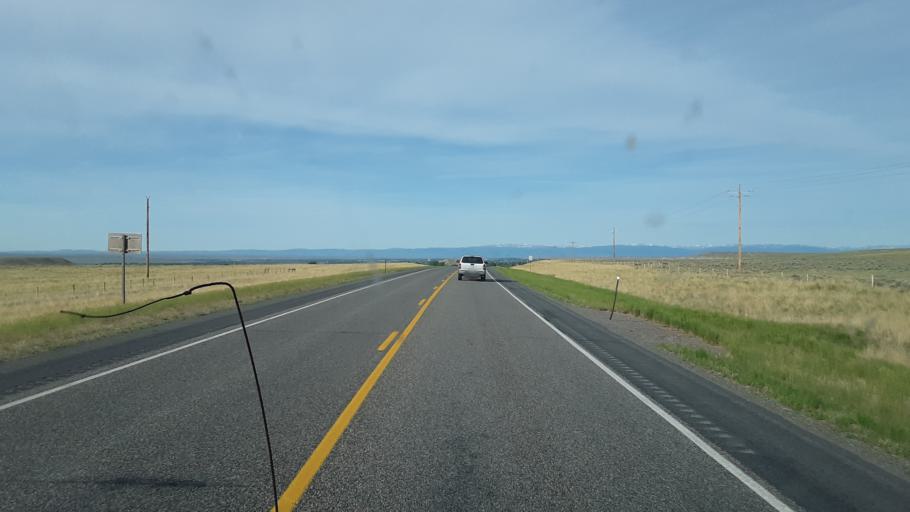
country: US
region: Wyoming
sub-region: Fremont County
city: Riverton
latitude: 43.1518
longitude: -108.2782
